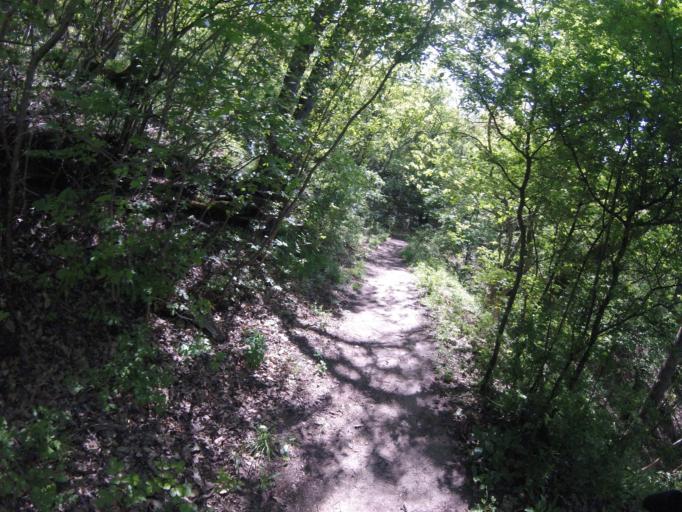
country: HU
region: Pest
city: Nagymaros
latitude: 47.7937
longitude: 18.9189
